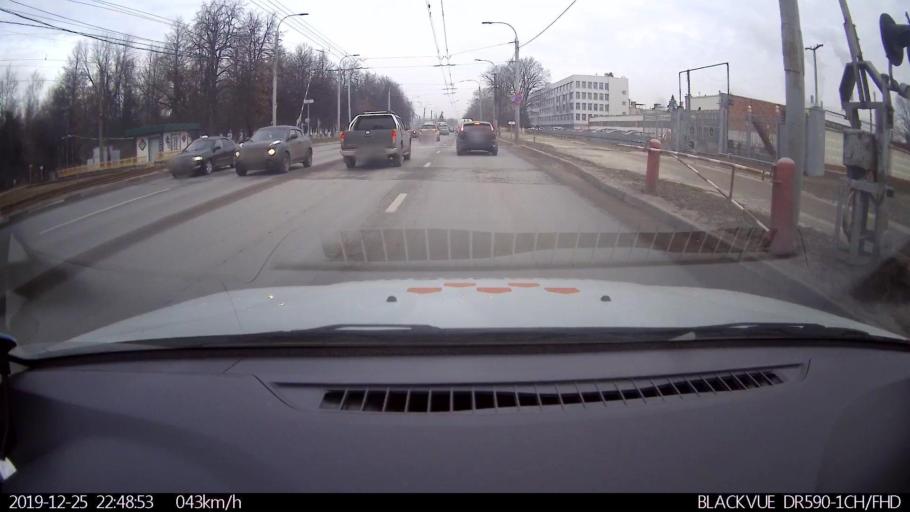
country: RU
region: Nizjnij Novgorod
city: Gorbatovka
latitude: 56.2447
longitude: 43.8711
